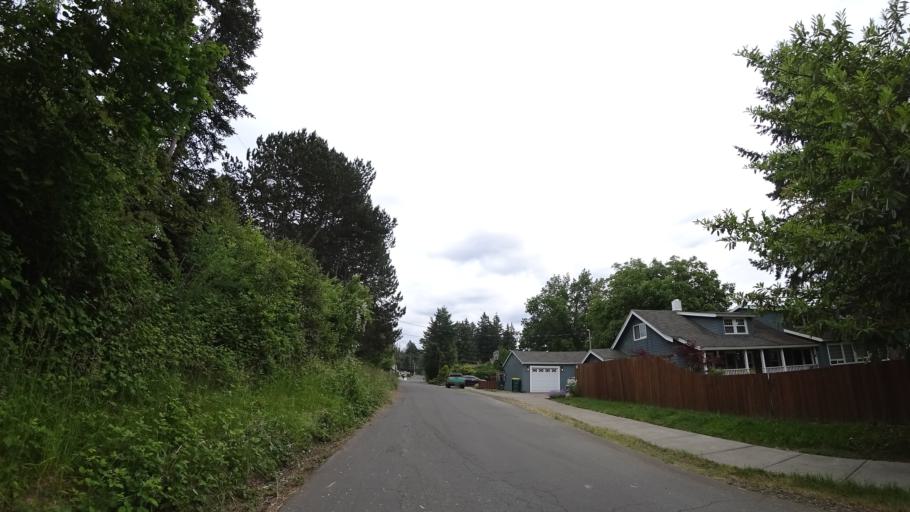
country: US
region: Oregon
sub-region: Washington County
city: Metzger
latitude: 45.4515
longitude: -122.7614
